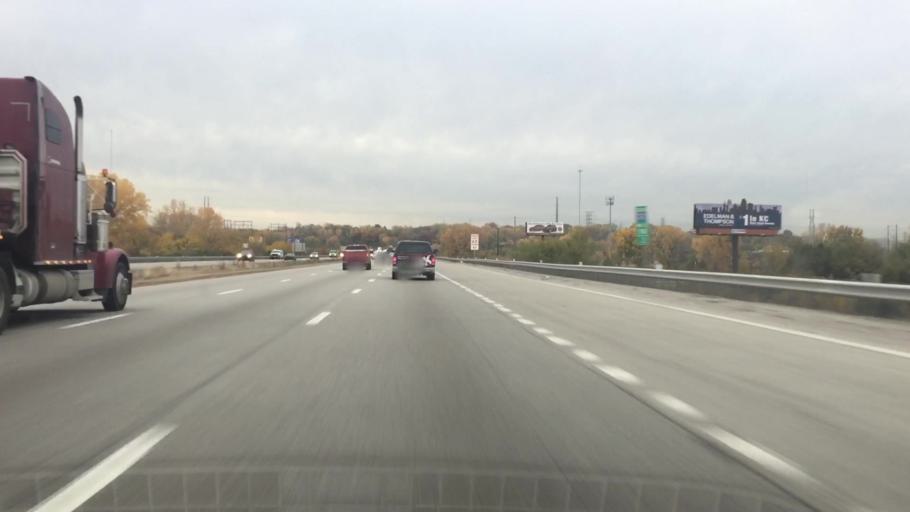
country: US
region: Missouri
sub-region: Jackson County
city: Sugar Creek
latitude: 39.1240
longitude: -94.4953
